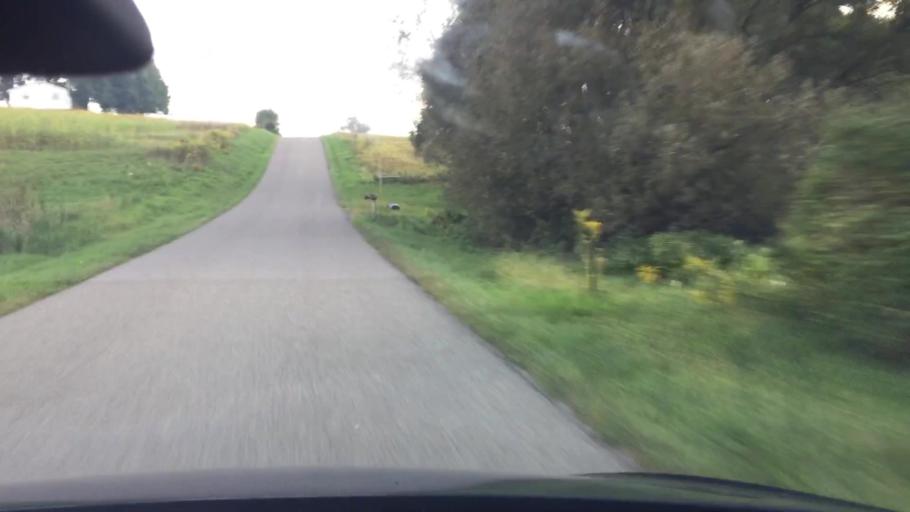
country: US
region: Pennsylvania
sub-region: Butler County
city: Oak Hills
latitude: 40.8149
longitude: -79.8917
